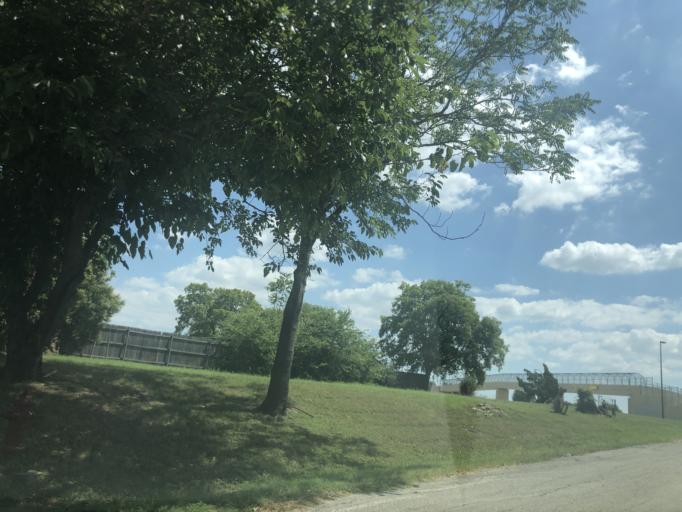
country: US
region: Texas
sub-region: Dallas County
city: Grand Prairie
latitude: 32.7474
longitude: -97.0277
